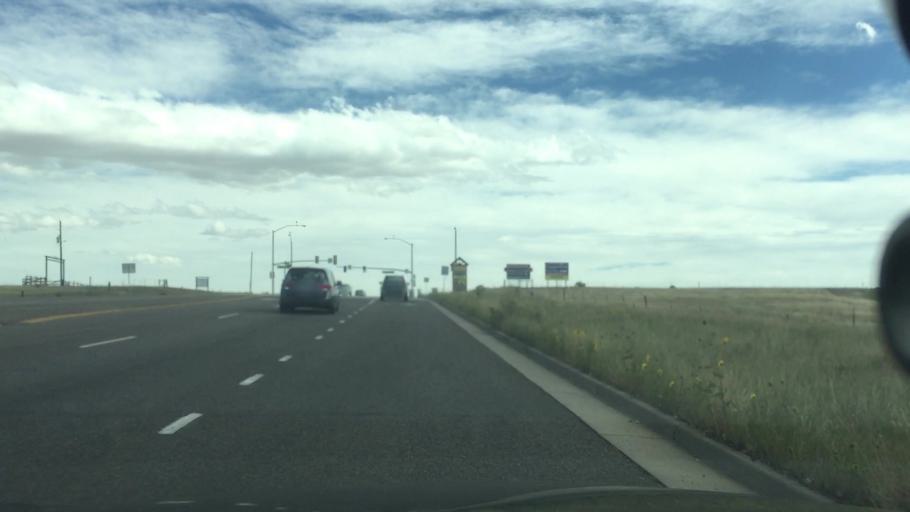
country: US
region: Colorado
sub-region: Arapahoe County
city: Dove Valley
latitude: 39.6529
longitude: -104.7370
